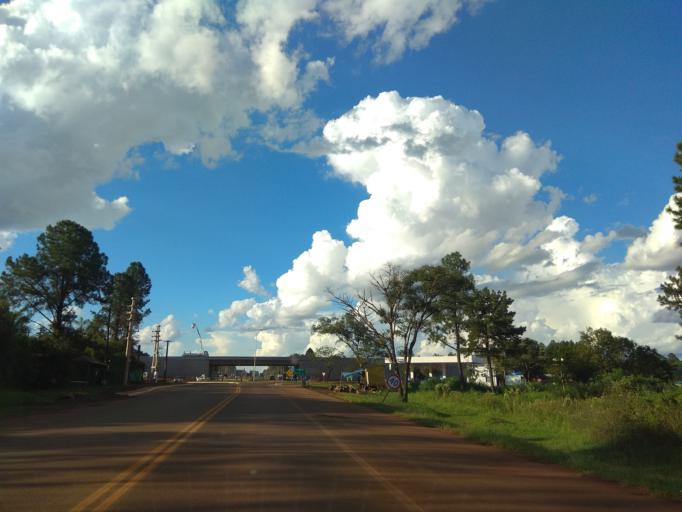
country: AR
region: Misiones
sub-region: Departamento de Candelaria
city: Candelaria
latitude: -27.4727
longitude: -55.7461
